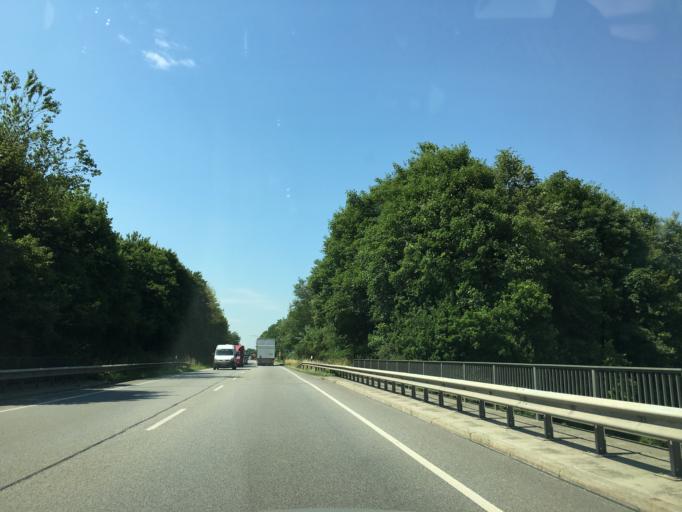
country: DE
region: Bavaria
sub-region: Upper Bavaria
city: Wasserburg am Inn
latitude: 48.0636
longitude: 12.2004
